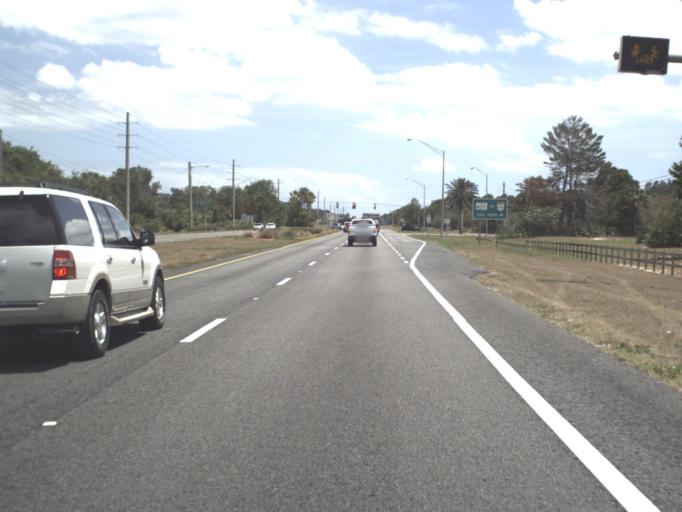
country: US
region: Florida
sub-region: Brevard County
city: Port Saint John
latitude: 28.5329
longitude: -80.8210
